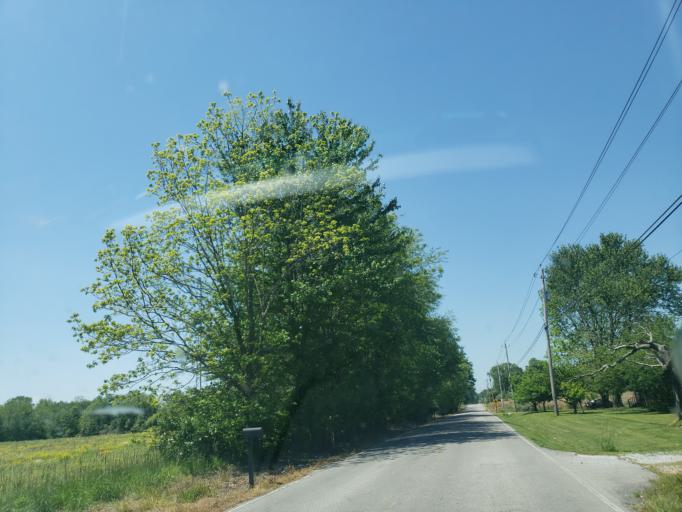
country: US
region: Alabama
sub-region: Madison County
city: Harvest
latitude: 34.9623
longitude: -86.7007
